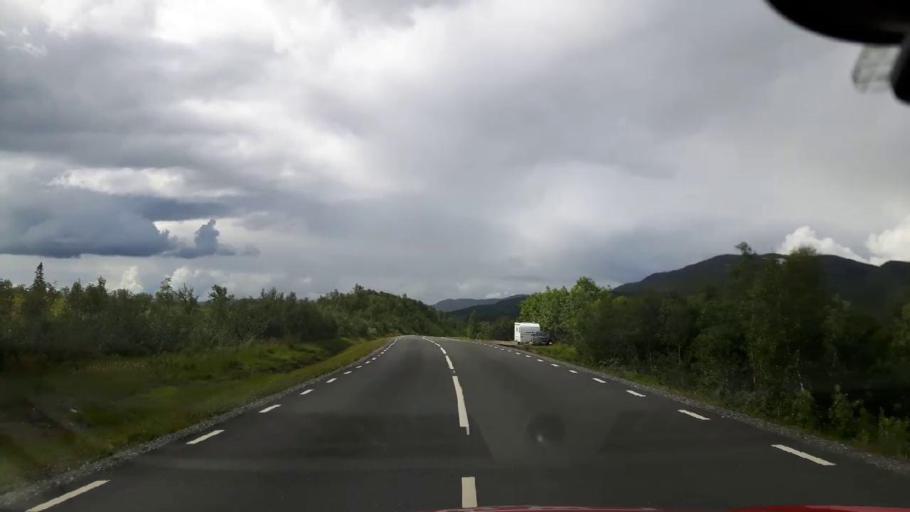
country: NO
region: Nordland
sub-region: Hattfjelldal
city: Hattfjelldal
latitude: 64.9941
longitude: 14.2306
